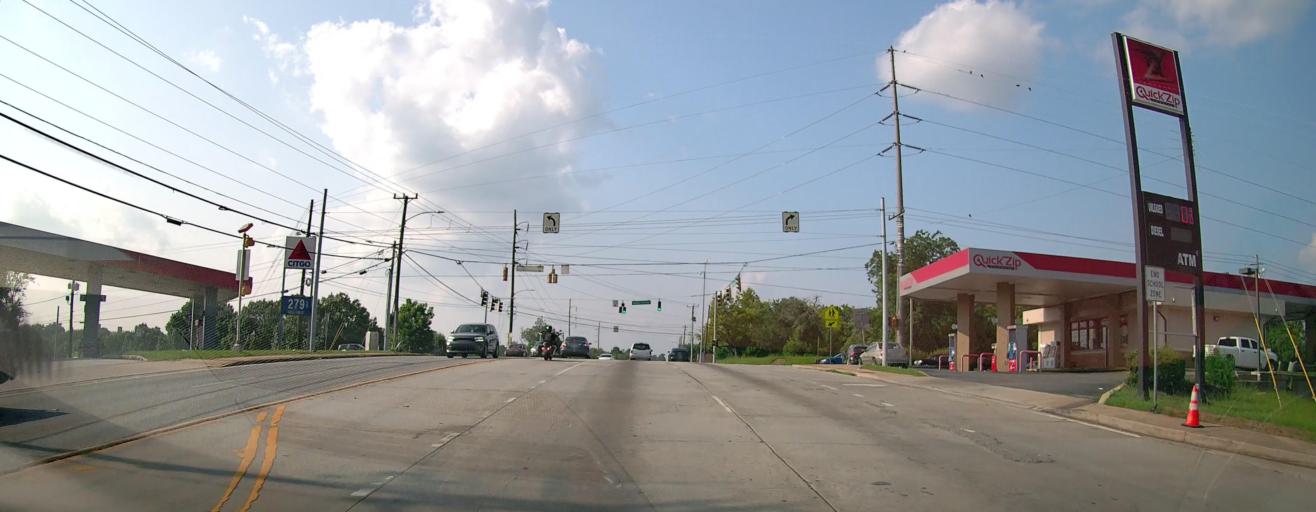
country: US
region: Georgia
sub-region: Bibb County
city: Macon
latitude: 32.8252
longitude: -83.6627
